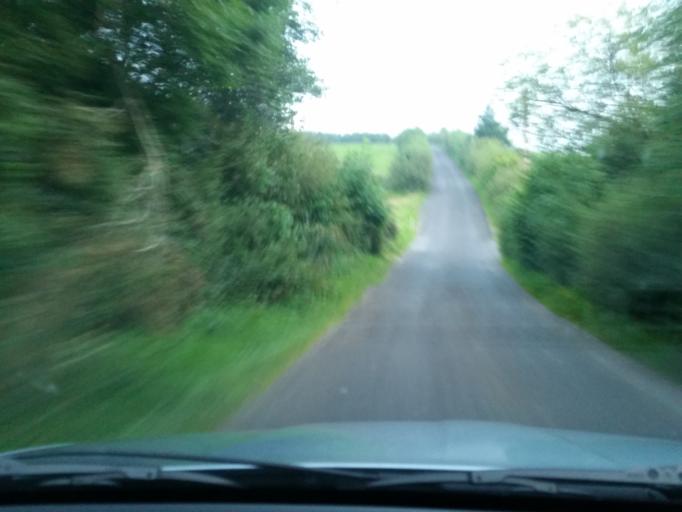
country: GB
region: Northern Ireland
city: Fivemiletown
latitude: 54.3129
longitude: -7.2959
